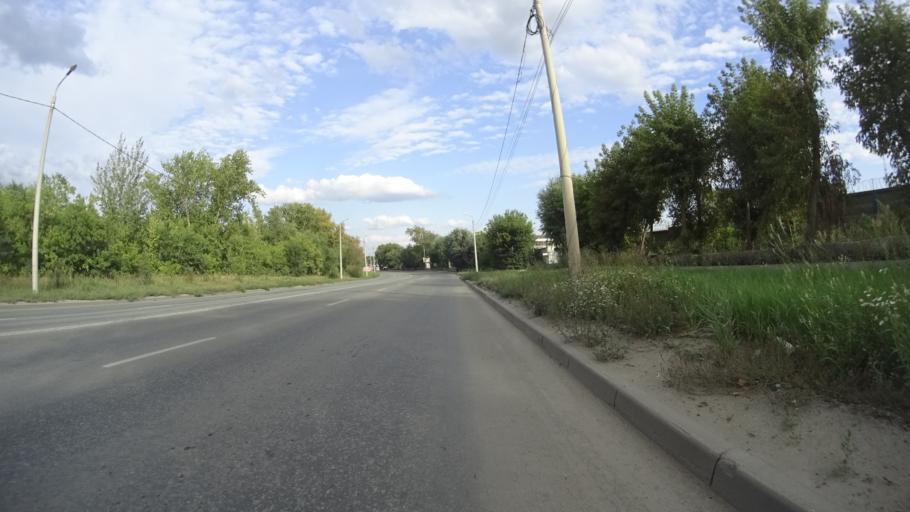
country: RU
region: Chelyabinsk
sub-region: Gorod Chelyabinsk
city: Chelyabinsk
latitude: 55.1963
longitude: 61.3750
